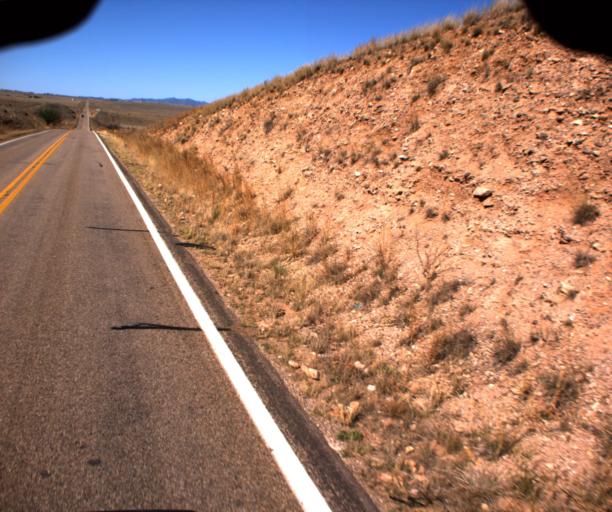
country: US
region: Arizona
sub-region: Cochise County
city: Huachuca City
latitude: 31.7062
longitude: -110.5818
